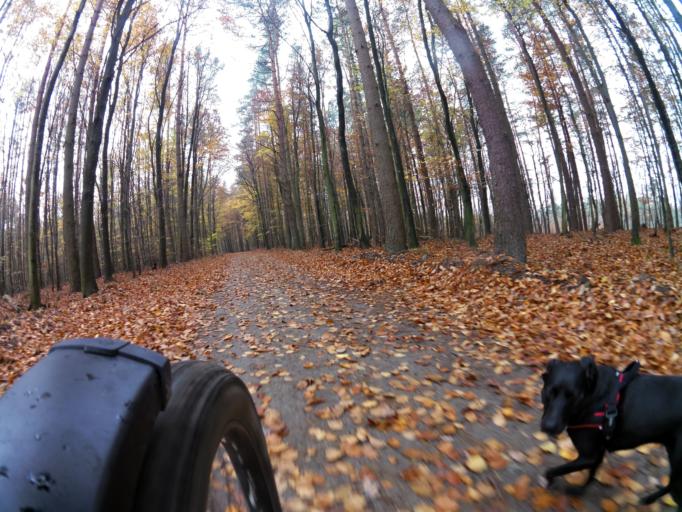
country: PL
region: Pomeranian Voivodeship
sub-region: Powiat pucki
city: Krokowa
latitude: 54.7738
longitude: 18.0918
